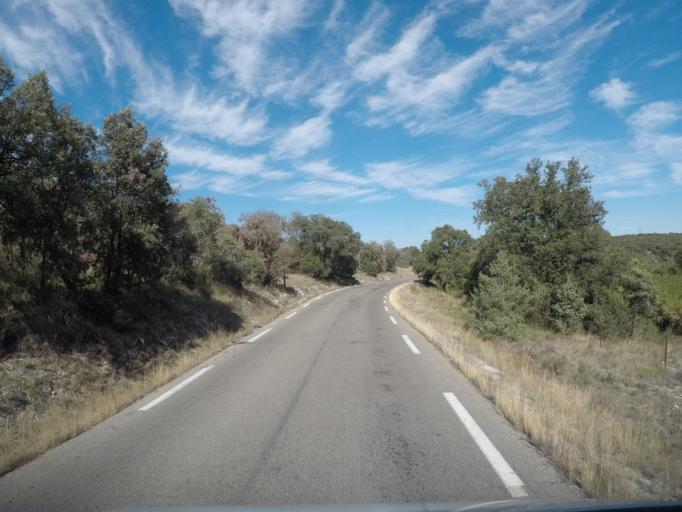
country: FR
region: Languedoc-Roussillon
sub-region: Departement du Gard
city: Anduze
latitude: 43.9991
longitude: 3.9756
